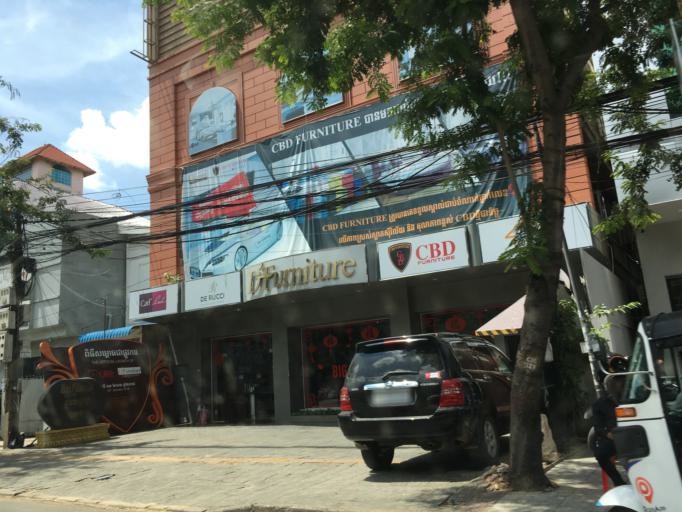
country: KH
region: Phnom Penh
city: Phnom Penh
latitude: 11.5440
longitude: 104.9178
